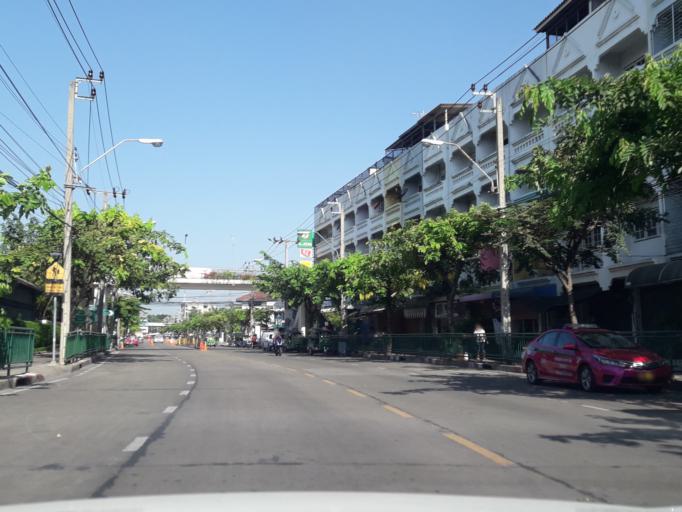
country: TH
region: Bangkok
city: Thon Buri
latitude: 13.7360
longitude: 100.4936
